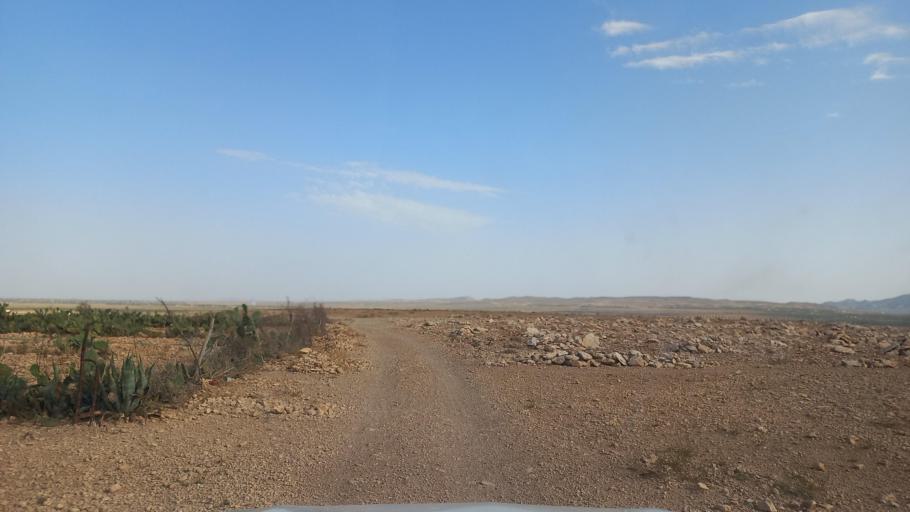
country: TN
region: Al Qasrayn
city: Kasserine
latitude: 35.2583
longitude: 8.9312
